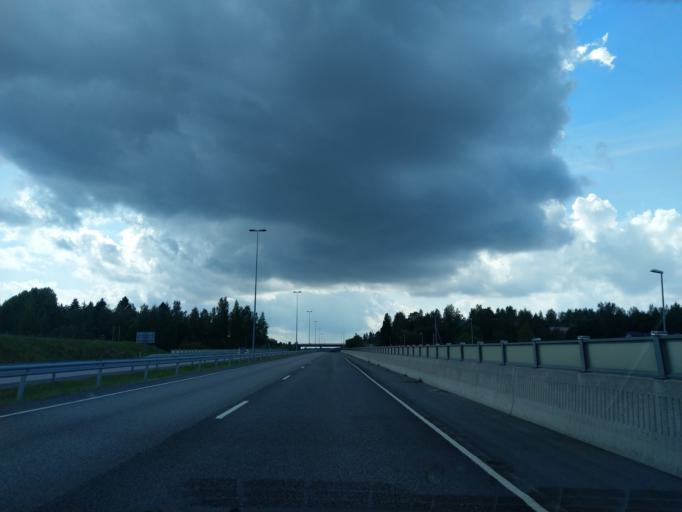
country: FI
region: South Karelia
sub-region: Imatra
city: Imatra
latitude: 61.1752
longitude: 28.7068
